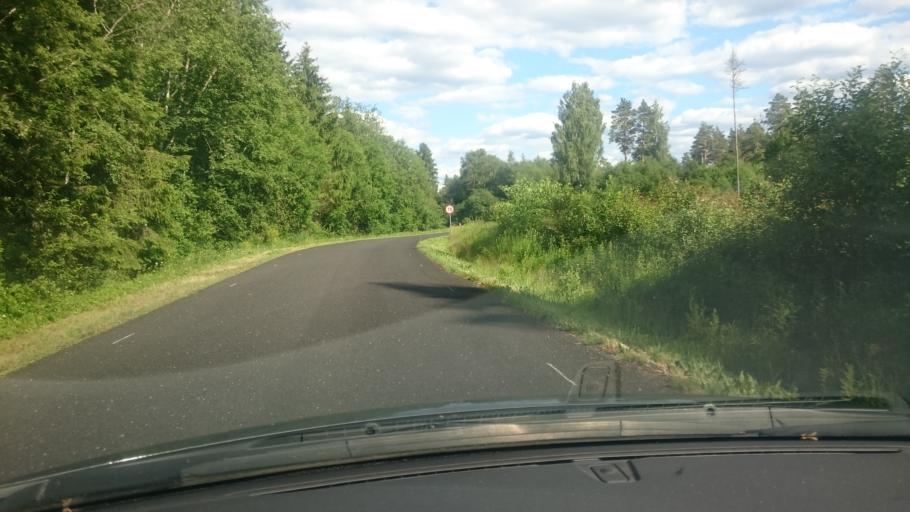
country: EE
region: Harju
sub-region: Rae vald
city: Vaida
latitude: 59.2286
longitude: 24.9948
